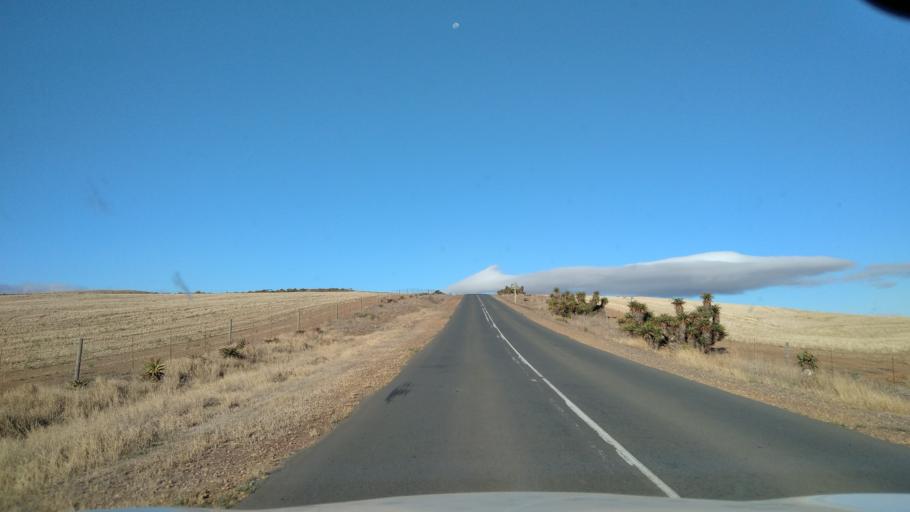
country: ZA
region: Western Cape
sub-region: Overberg District Municipality
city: Caledon
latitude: -34.1708
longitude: 19.2869
